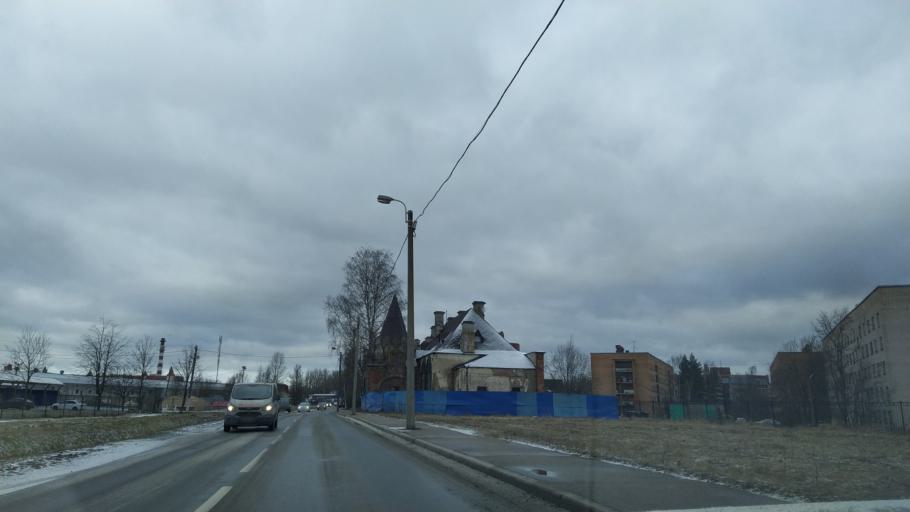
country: RU
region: St.-Petersburg
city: Pushkin
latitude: 59.7305
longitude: 30.3849
